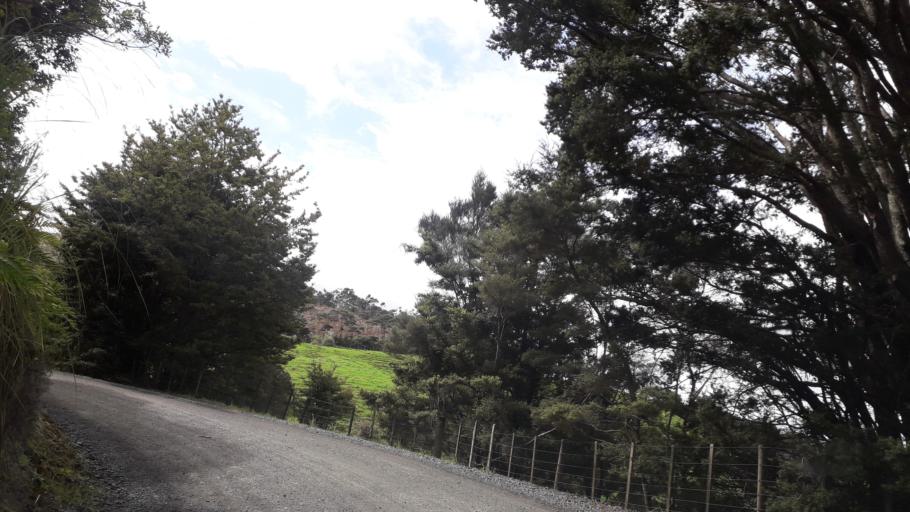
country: NZ
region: Northland
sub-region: Far North District
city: Kaitaia
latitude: -35.2271
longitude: 173.2697
